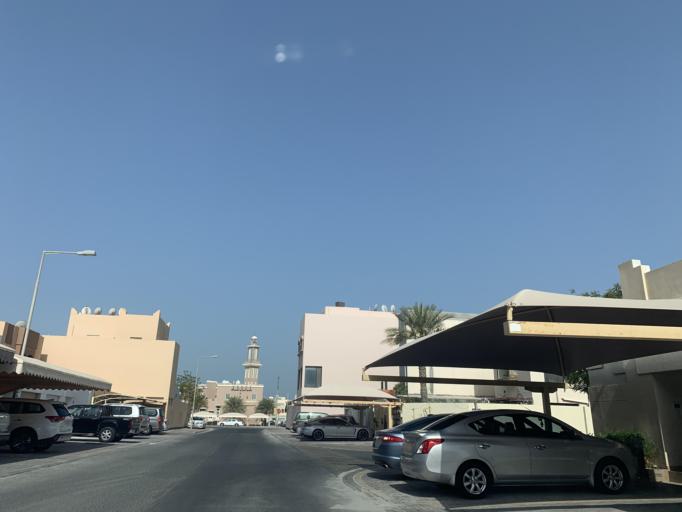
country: BH
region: Muharraq
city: Al Muharraq
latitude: 26.2706
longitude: 50.5986
